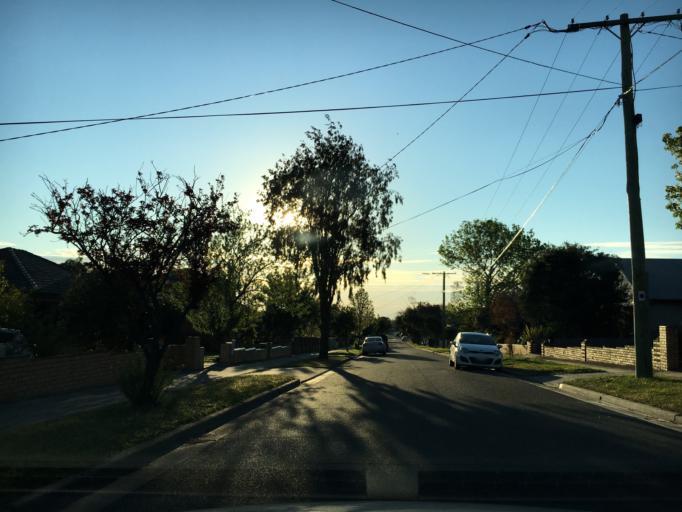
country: AU
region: Victoria
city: Clayton
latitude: -37.9056
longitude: 145.1103
